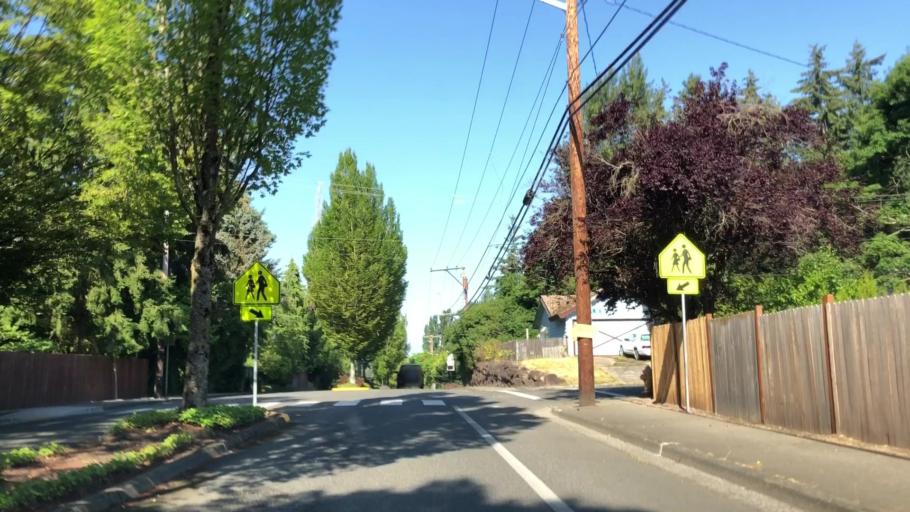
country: US
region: Washington
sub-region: King County
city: Eastgate
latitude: 47.6098
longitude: -122.1351
